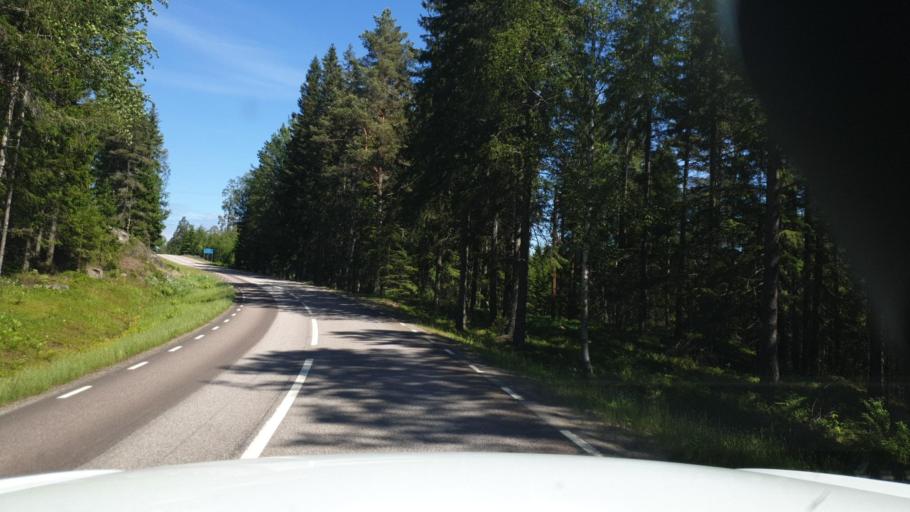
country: SE
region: Vaermland
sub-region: Eda Kommun
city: Amotfors
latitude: 59.6340
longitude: 12.3511
